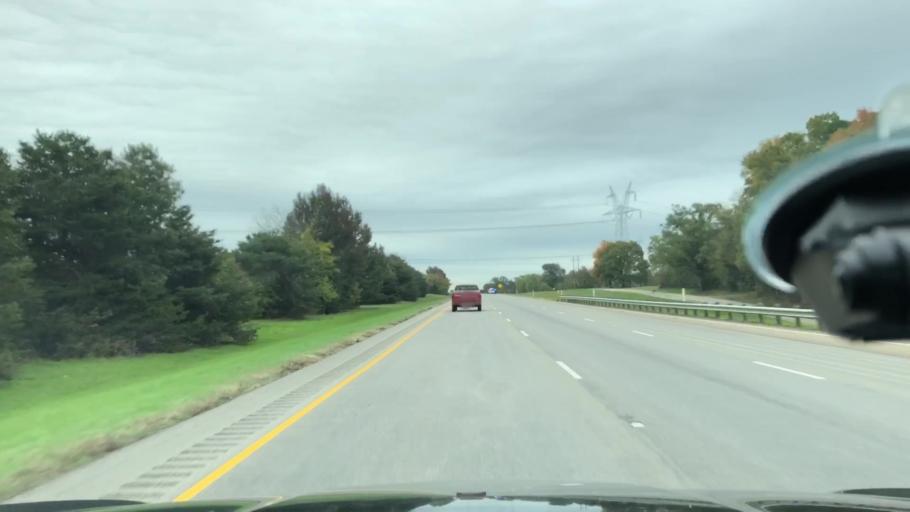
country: US
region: Texas
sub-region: Franklin County
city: Mount Vernon
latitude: 33.1624
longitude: -95.1680
